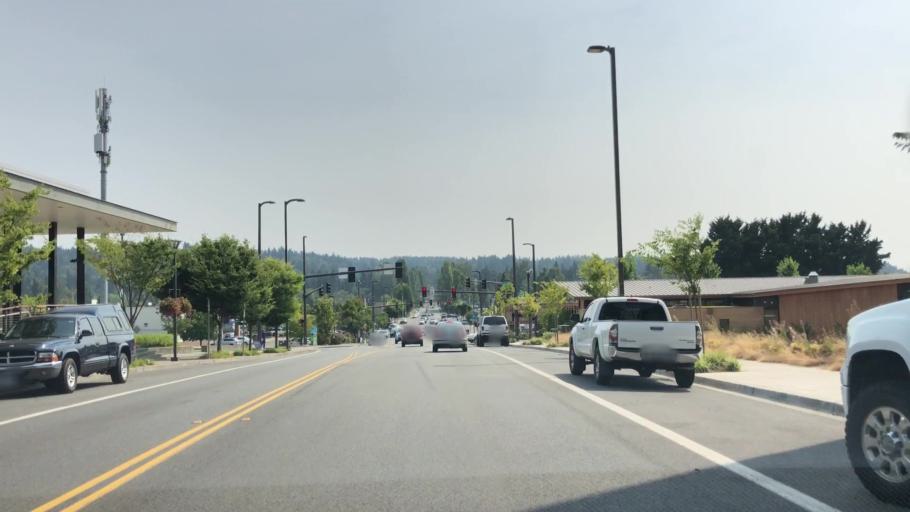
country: US
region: Washington
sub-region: King County
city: Kenmore
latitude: 47.7604
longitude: -122.2497
